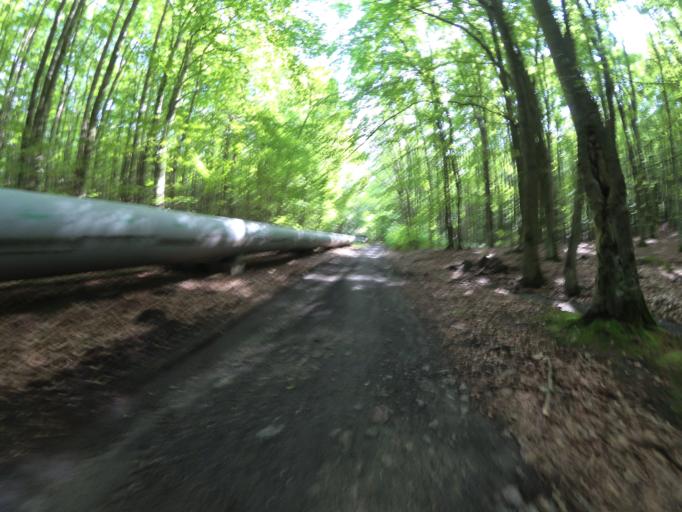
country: PL
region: Pomeranian Voivodeship
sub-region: Gdynia
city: Wielki Kack
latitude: 54.5078
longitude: 18.4894
